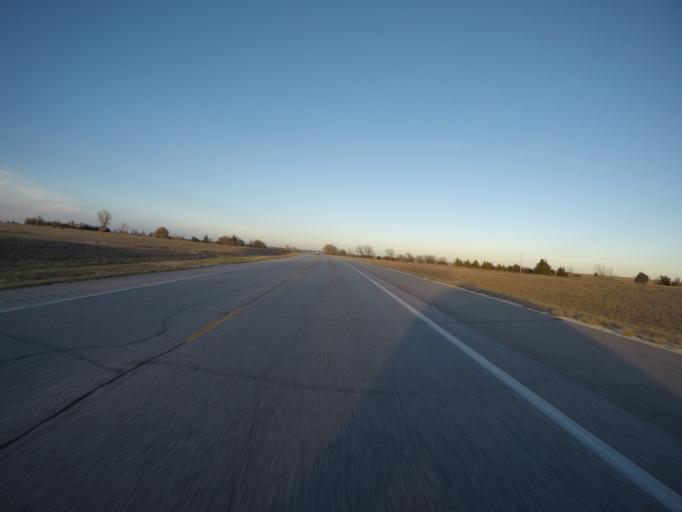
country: US
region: Kansas
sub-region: Marion County
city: Peabody
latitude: 38.1389
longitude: -97.2322
